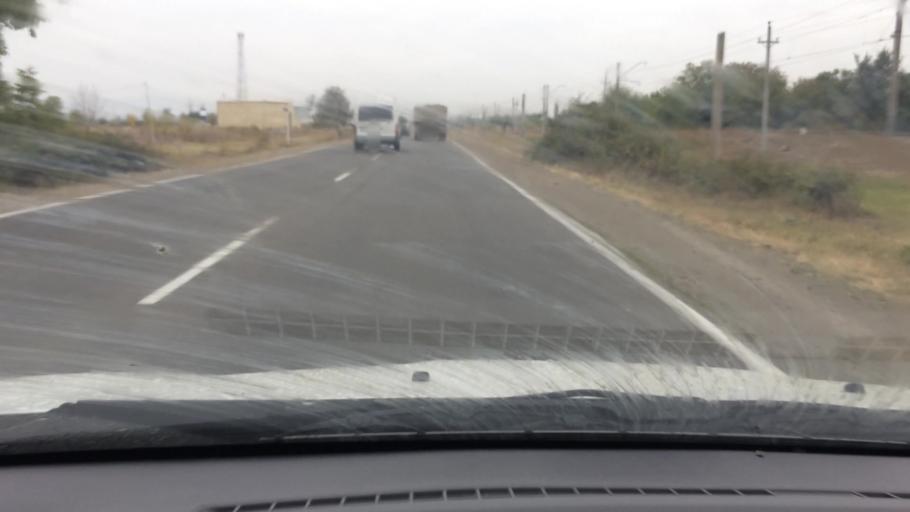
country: GE
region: Kvemo Kartli
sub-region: Marneuli
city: Marneuli
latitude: 41.4331
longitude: 44.8207
